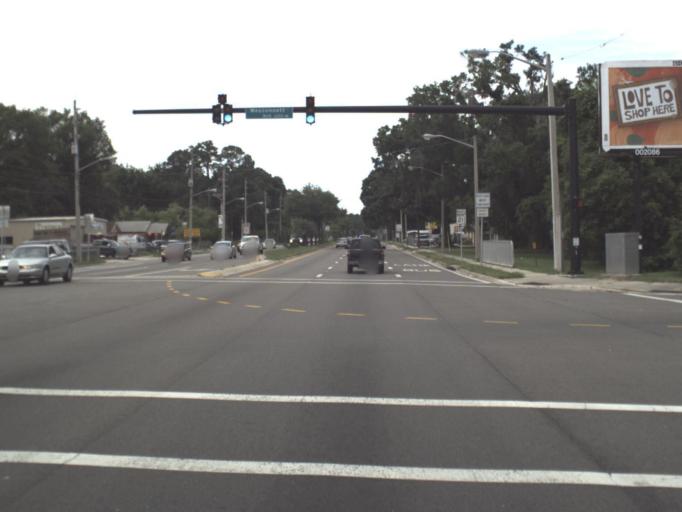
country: US
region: Florida
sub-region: Clay County
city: Bellair-Meadowbrook Terrace
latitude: 30.2355
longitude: -81.7398
